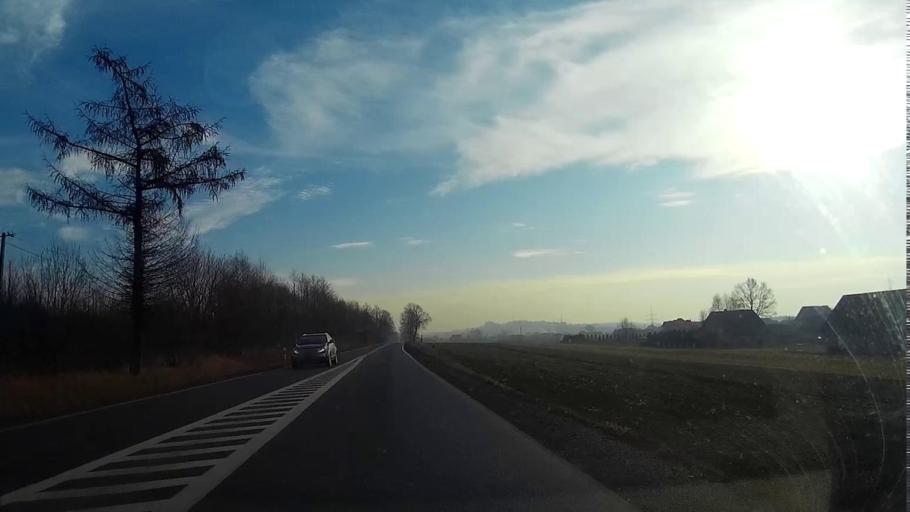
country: PL
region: Lesser Poland Voivodeship
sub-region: Powiat chrzanowski
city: Kwaczala
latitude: 50.0657
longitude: 19.4818
